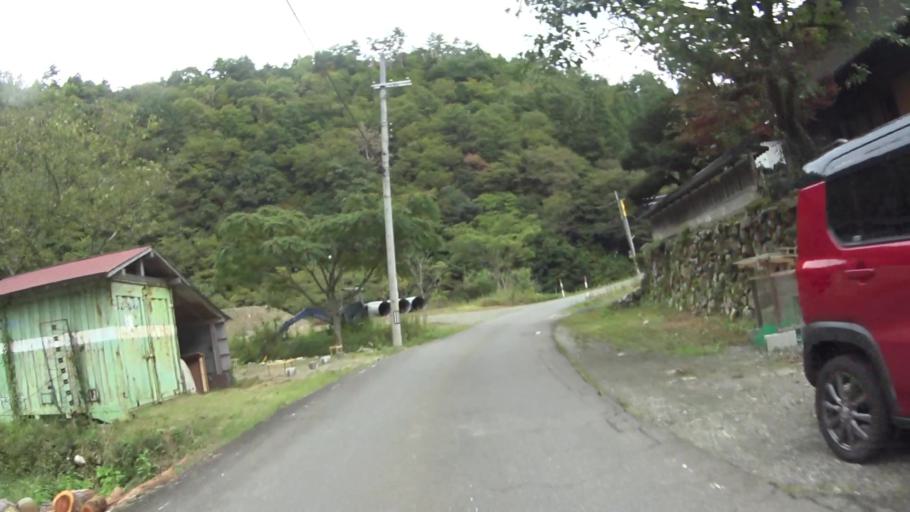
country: JP
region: Fukui
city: Obama
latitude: 35.2939
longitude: 135.6942
